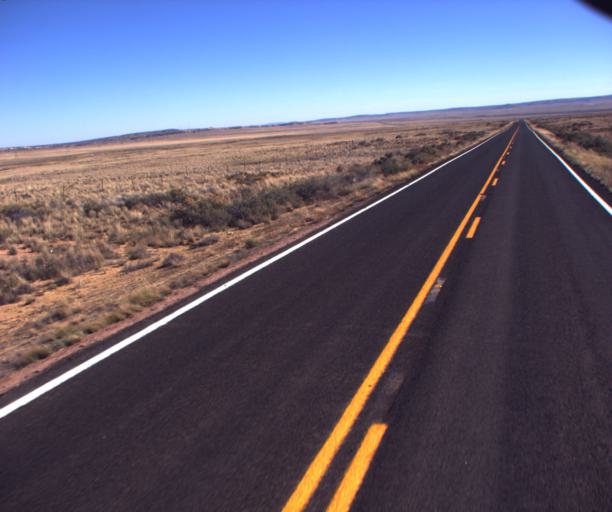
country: US
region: Arizona
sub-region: Coconino County
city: Tuba City
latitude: 35.9703
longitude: -110.8220
